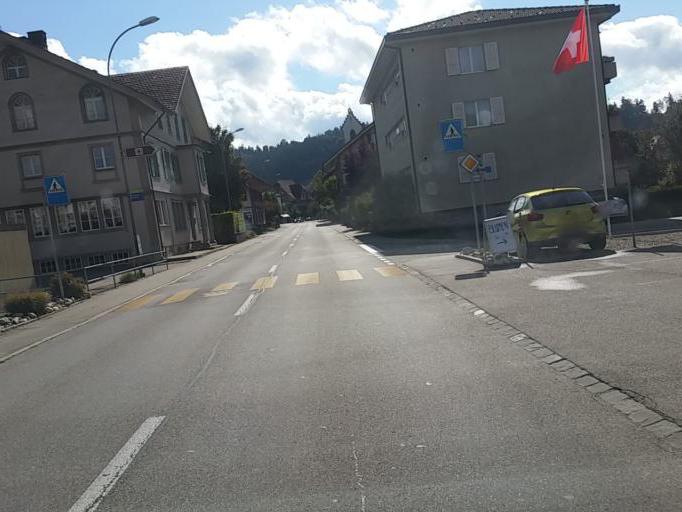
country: CH
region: Bern
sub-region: Emmental District
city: Sumiswald
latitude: 47.0300
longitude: 7.7431
